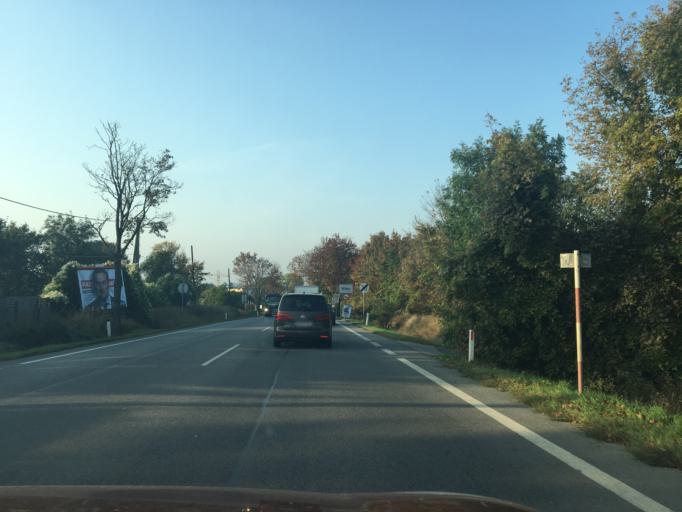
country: AT
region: Lower Austria
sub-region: Politischer Bezirk Korneuburg
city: Hagenbrunn
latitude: 48.3052
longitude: 16.4250
